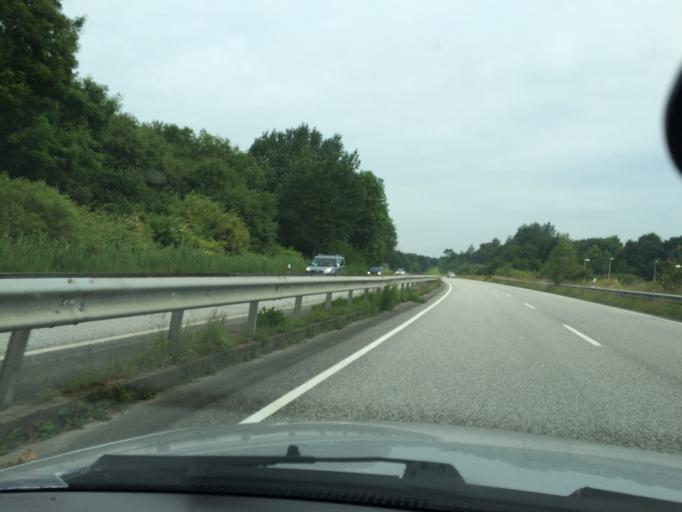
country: DE
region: Schleswig-Holstein
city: Harrislee
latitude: 54.7994
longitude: 9.4088
